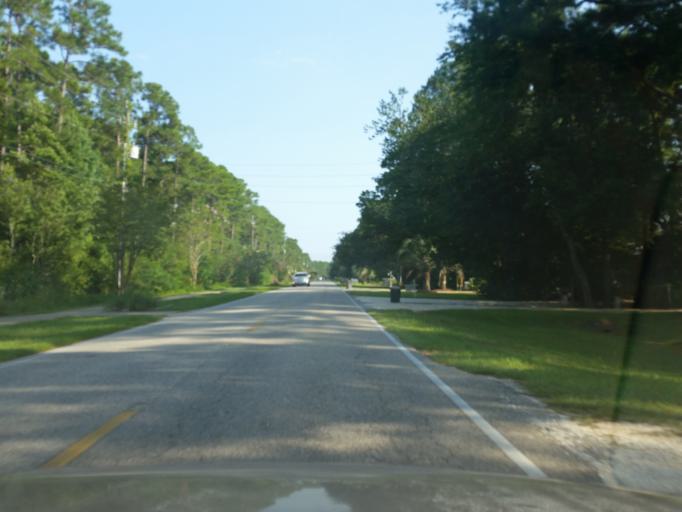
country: US
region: Alabama
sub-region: Baldwin County
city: Point Clear
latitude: 30.4535
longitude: -87.9150
